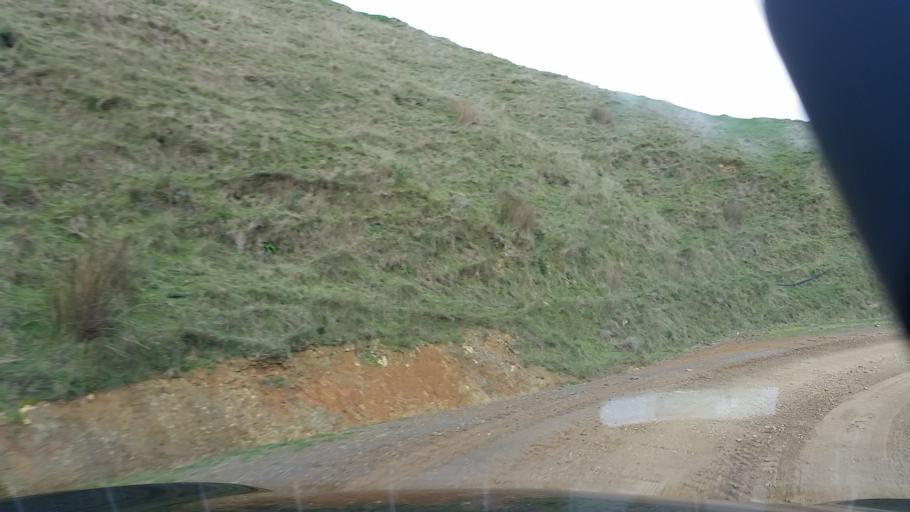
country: NZ
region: Marlborough
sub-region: Marlborough District
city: Picton
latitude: -40.9896
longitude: 173.8320
